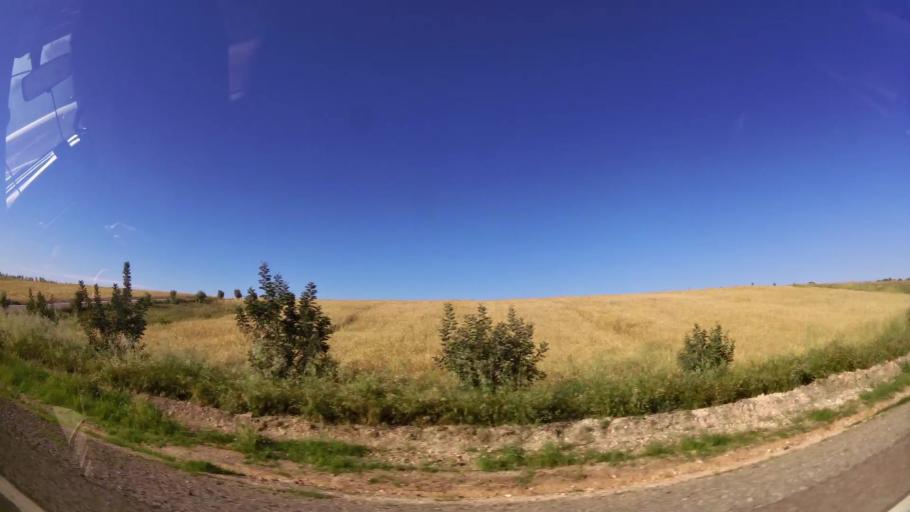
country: MA
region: Oriental
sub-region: Berkane-Taourirt
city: Ahfir
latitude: 34.9797
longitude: -2.1368
